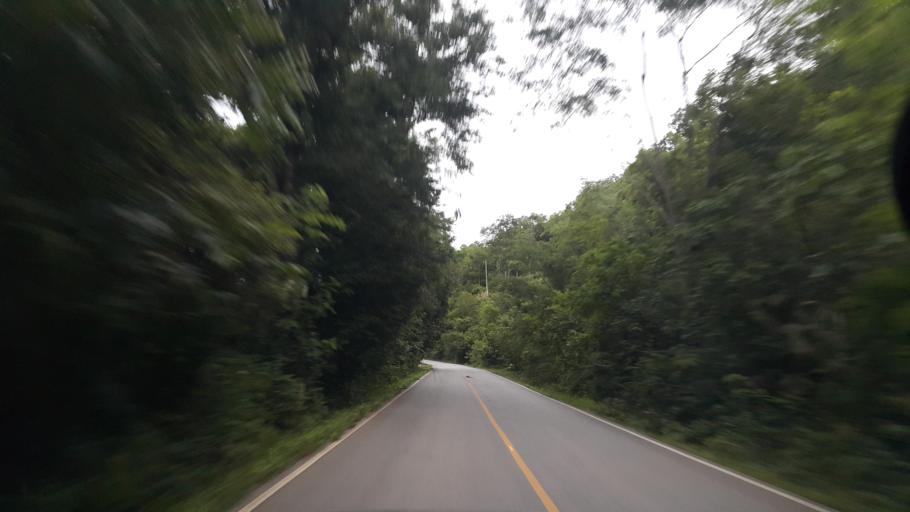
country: TH
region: Loei
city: Na Haeo
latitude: 17.5301
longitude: 101.2005
